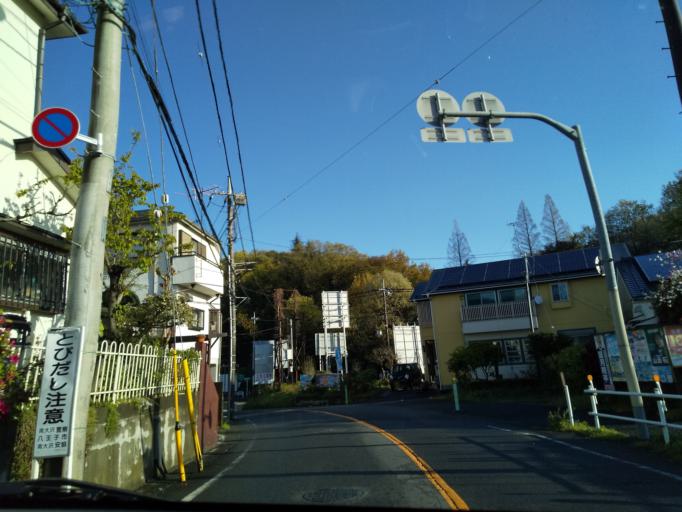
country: JP
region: Tokyo
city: Hachioji
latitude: 35.6326
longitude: 139.3649
